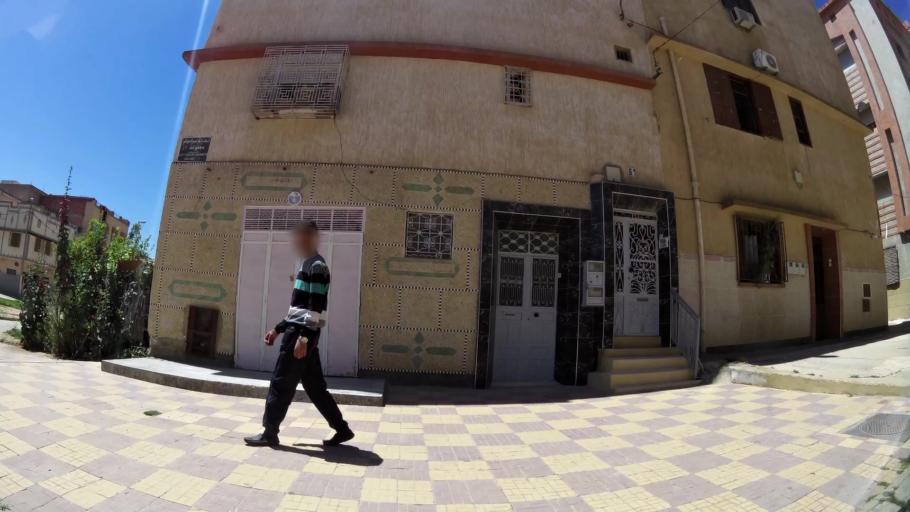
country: MA
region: Meknes-Tafilalet
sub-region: Meknes
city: Meknes
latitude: 33.8785
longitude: -5.5661
